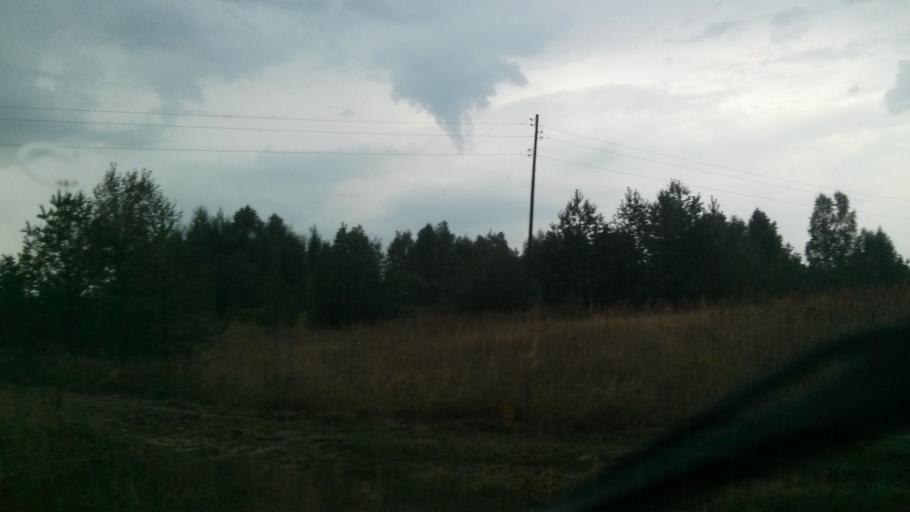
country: RU
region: Nizjnij Novgorod
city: Shimorskoye
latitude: 55.3177
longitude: 41.8621
